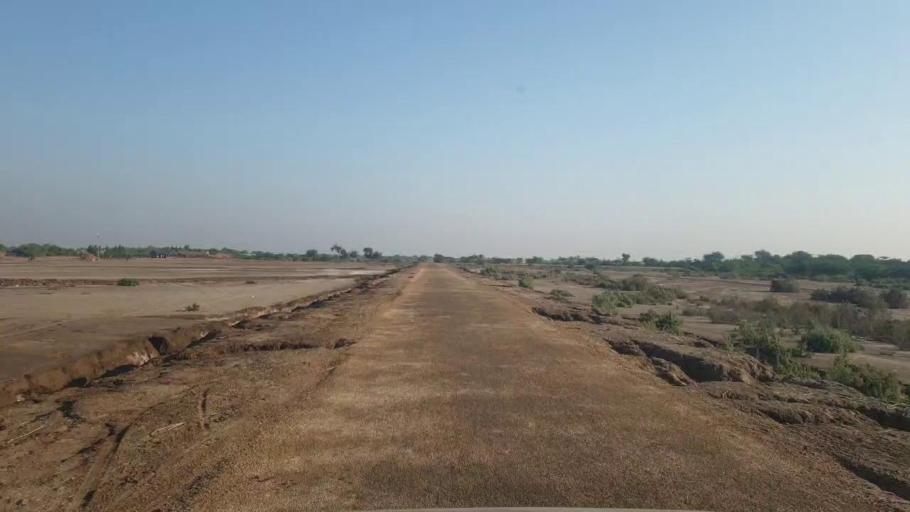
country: PK
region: Sindh
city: Badin
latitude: 24.7219
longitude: 68.8625
